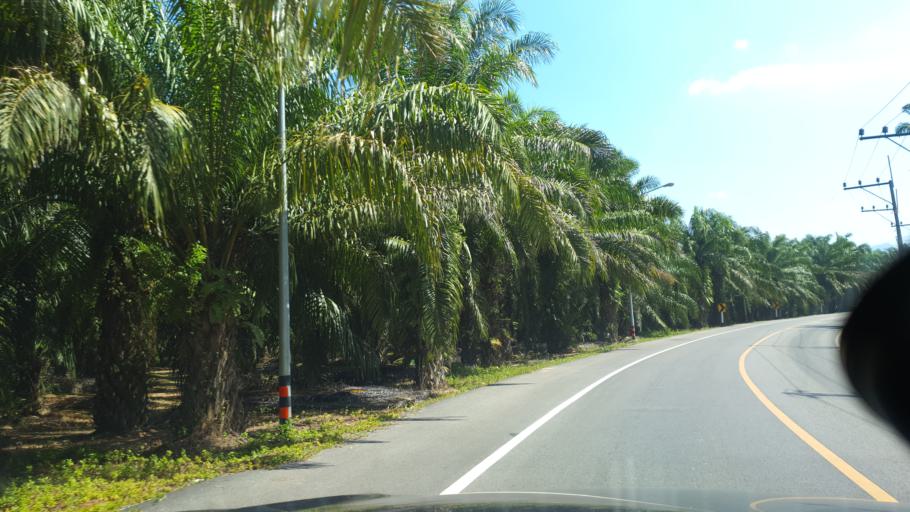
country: TH
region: Krabi
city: Khlong Thom
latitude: 7.9533
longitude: 99.2029
